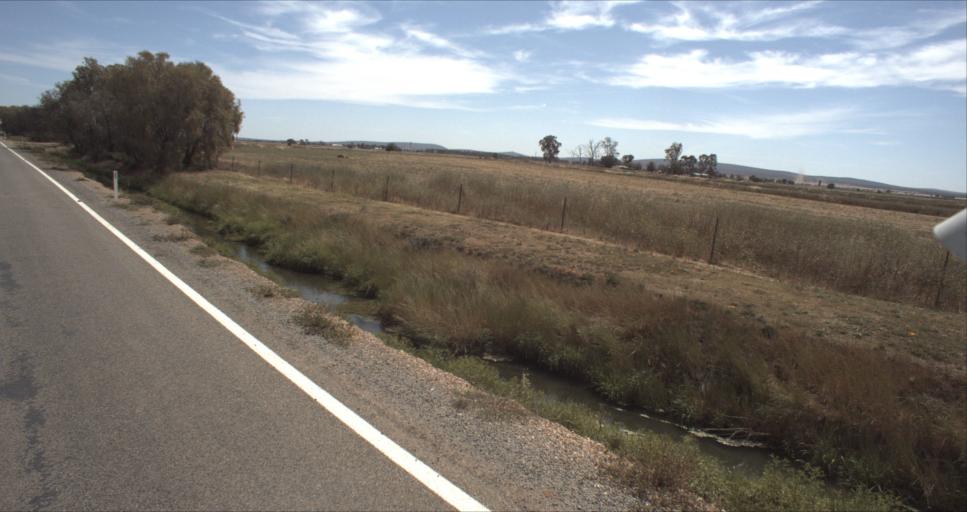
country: AU
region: New South Wales
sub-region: Leeton
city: Leeton
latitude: -34.5564
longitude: 146.4398
